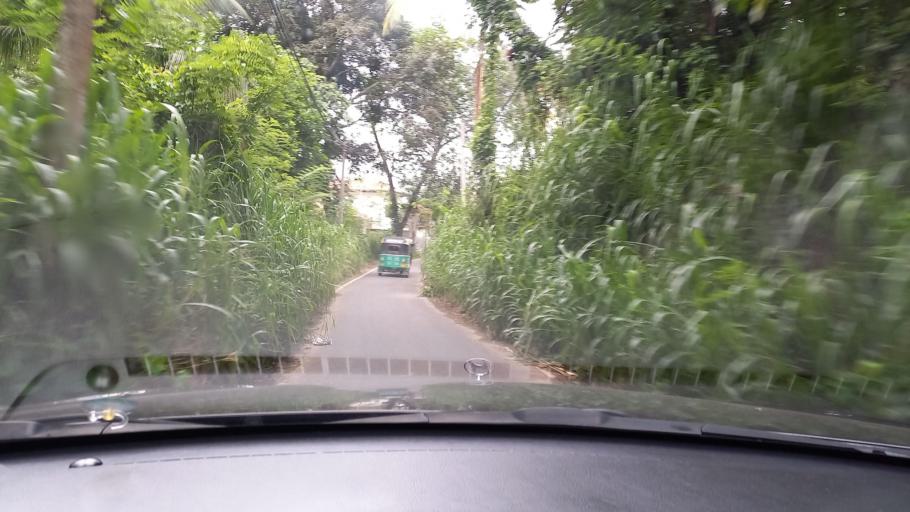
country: LK
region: Central
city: Kadugannawa
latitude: 7.2601
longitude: 80.3548
